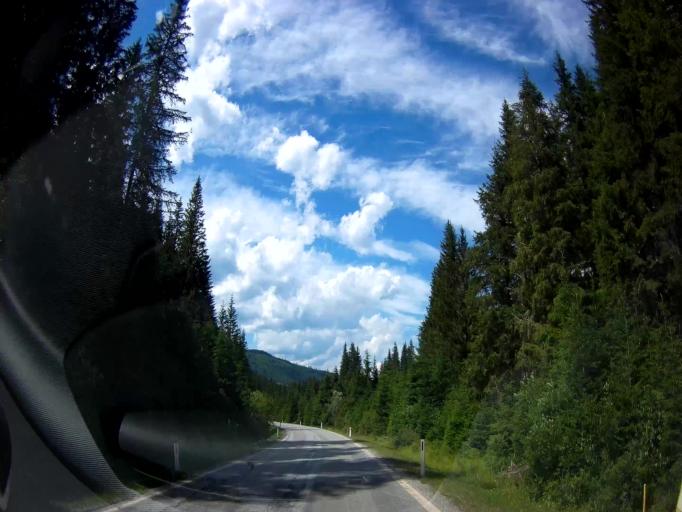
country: AT
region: Styria
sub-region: Politischer Bezirk Murau
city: Stadl an der Mur
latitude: 47.0002
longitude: 14.0141
